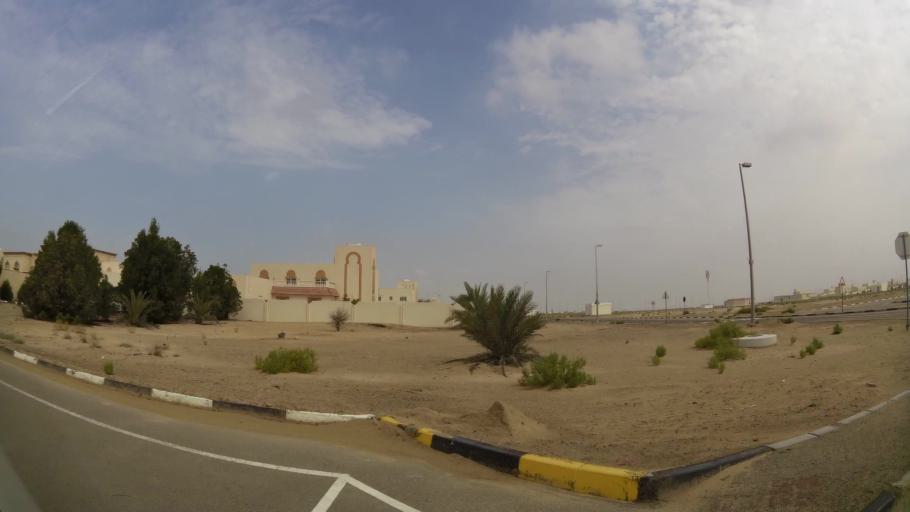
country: AE
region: Abu Dhabi
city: Abu Dhabi
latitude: 24.6327
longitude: 54.6769
